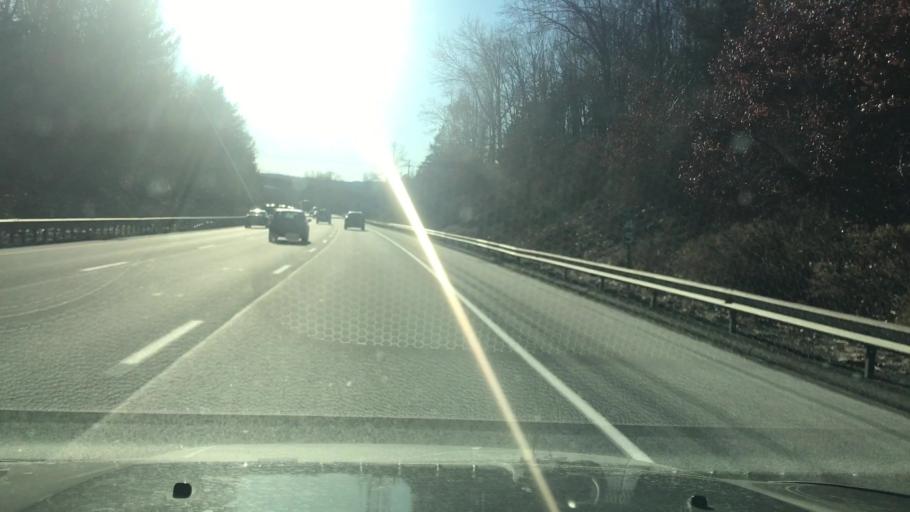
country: US
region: Connecticut
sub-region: Hartford County
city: Plainville
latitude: 41.6206
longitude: -72.8923
